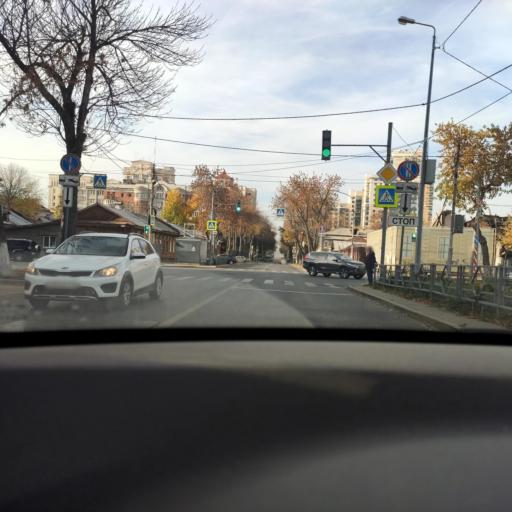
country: RU
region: Samara
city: Samara
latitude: 53.1999
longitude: 50.1195
